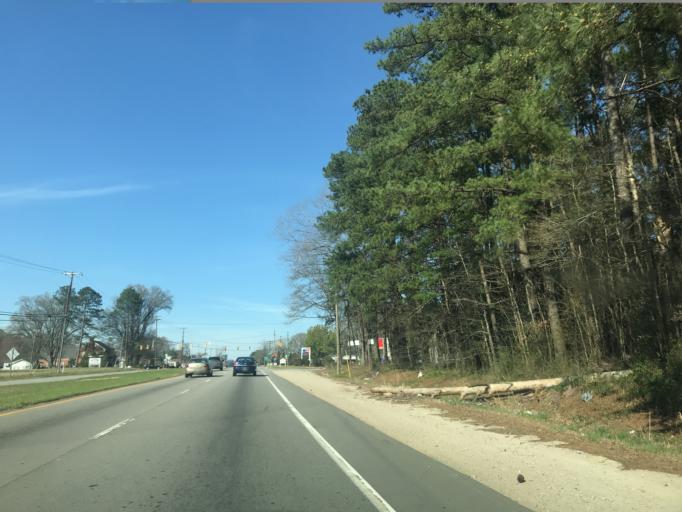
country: US
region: North Carolina
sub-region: Wake County
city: Garner
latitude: 35.7108
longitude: -78.6583
